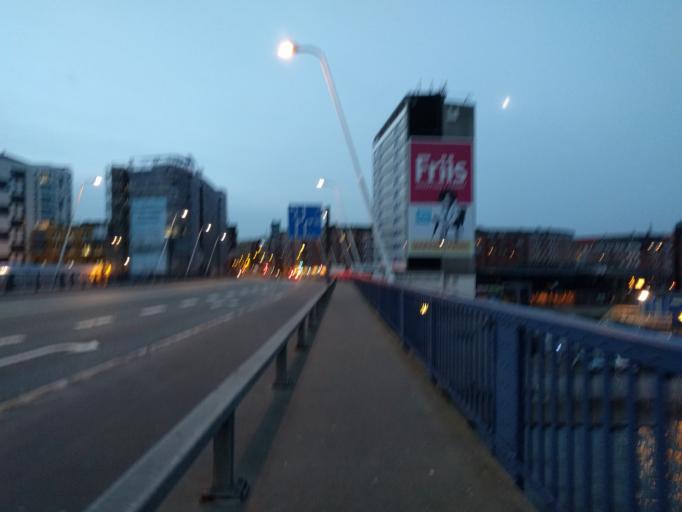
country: DK
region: North Denmark
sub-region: Alborg Kommune
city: Aalborg
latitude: 57.0533
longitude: 9.9181
